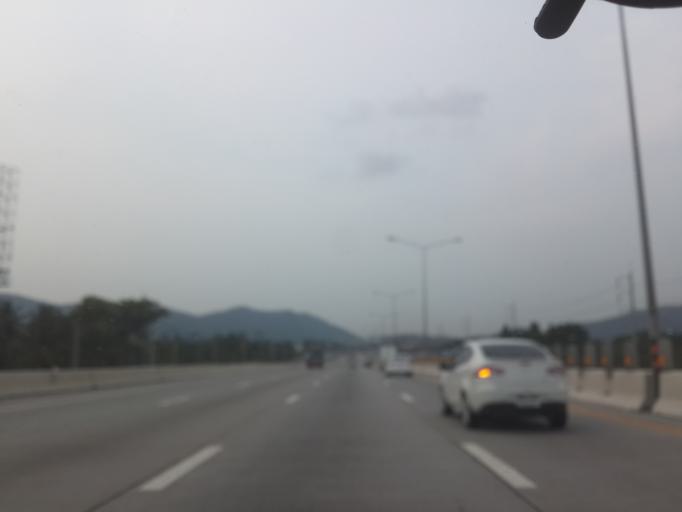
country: TH
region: Chon Buri
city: Si Racha
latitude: 13.2315
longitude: 101.0003
